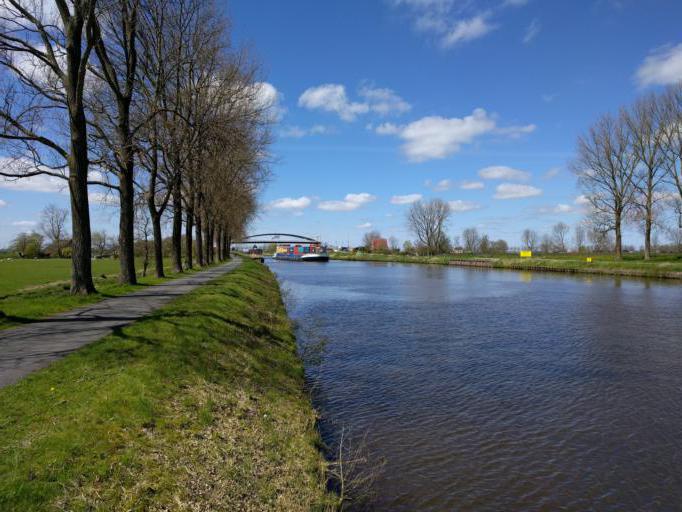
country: NL
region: Groningen
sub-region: Gemeente Zuidhorn
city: Aduard
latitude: 53.2575
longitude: 6.5066
